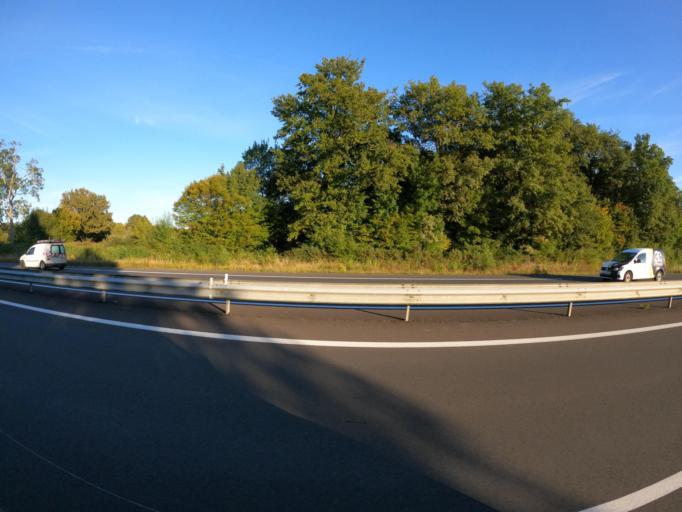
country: FR
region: Pays de la Loire
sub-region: Departement de la Vendee
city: Saint-Fulgent
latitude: 46.8476
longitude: -1.1472
